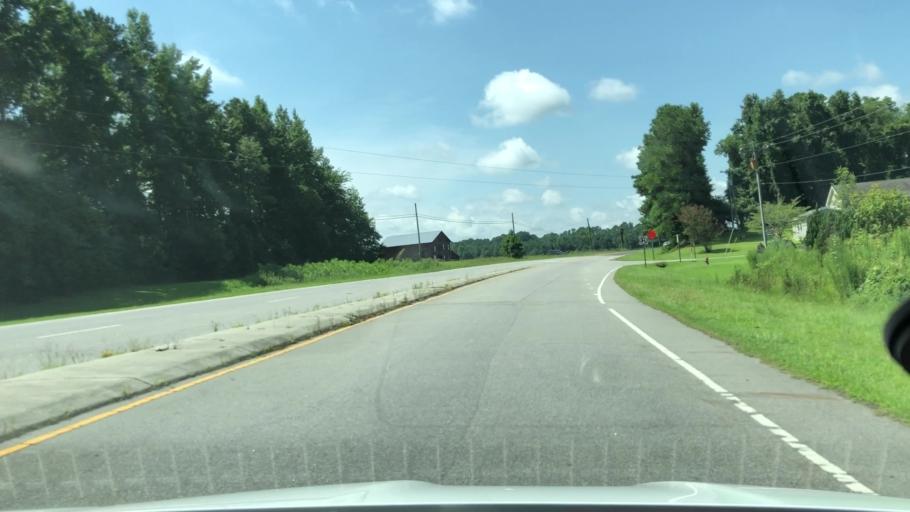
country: US
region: North Carolina
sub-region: Martin County
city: Williamston
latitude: 35.7835
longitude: -77.0602
